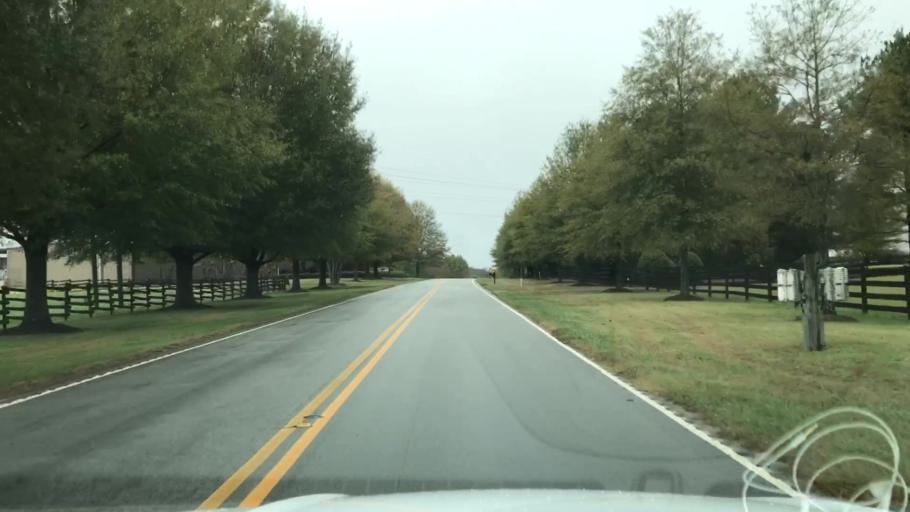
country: US
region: South Carolina
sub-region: Spartanburg County
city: Roebuck
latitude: 34.8121
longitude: -81.9231
